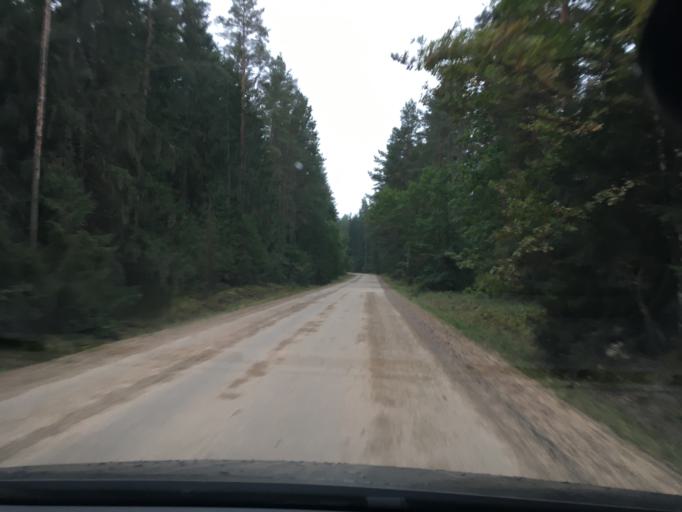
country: LV
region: Kuldigas Rajons
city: Kuldiga
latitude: 56.9895
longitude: 21.9743
